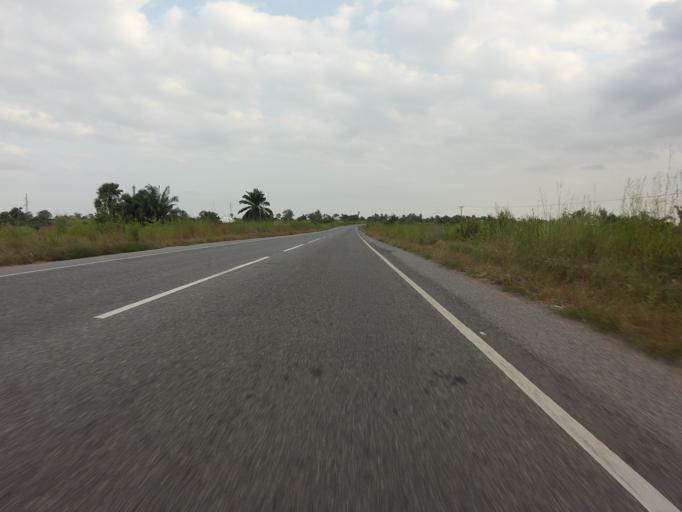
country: GH
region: Volta
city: Ho
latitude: 6.2556
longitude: 0.5504
